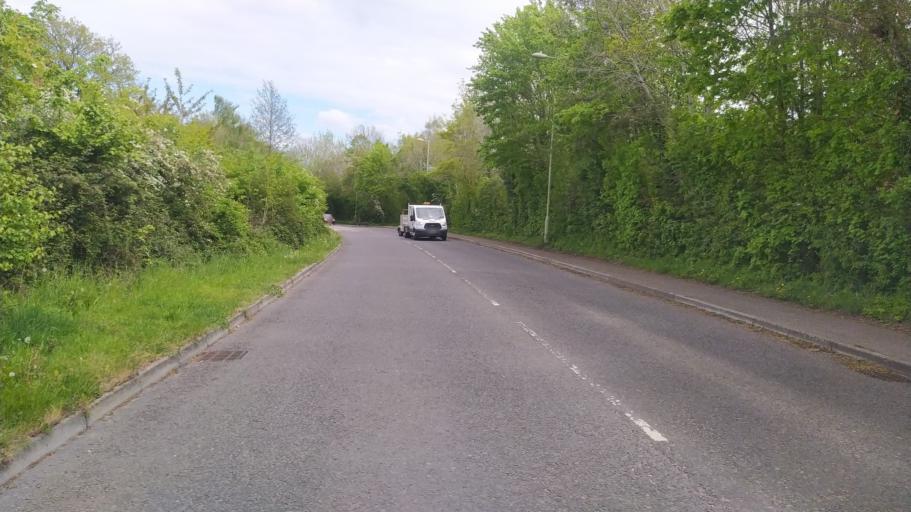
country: GB
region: England
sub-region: Hampshire
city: Totton
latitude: 50.9230
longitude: -1.5208
